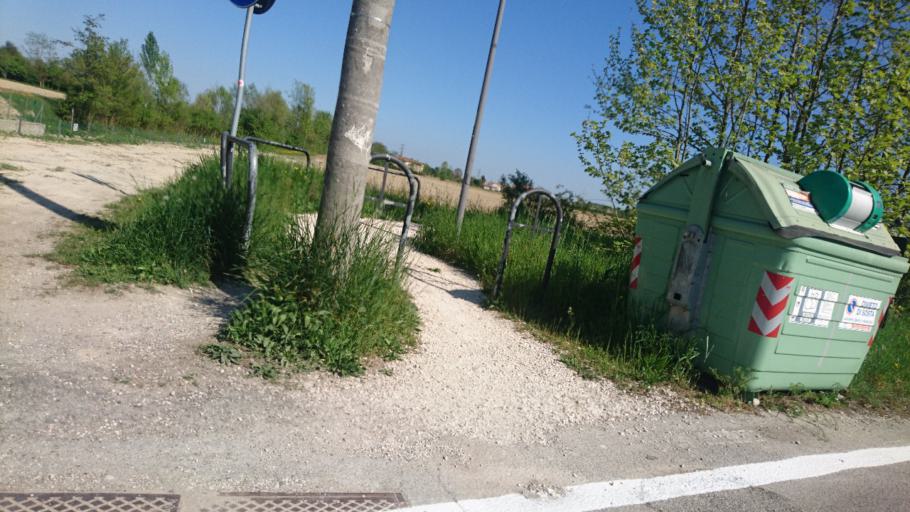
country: IT
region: Veneto
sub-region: Provincia di Treviso
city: Mogliano Veneto
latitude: 45.5182
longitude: 12.2571
